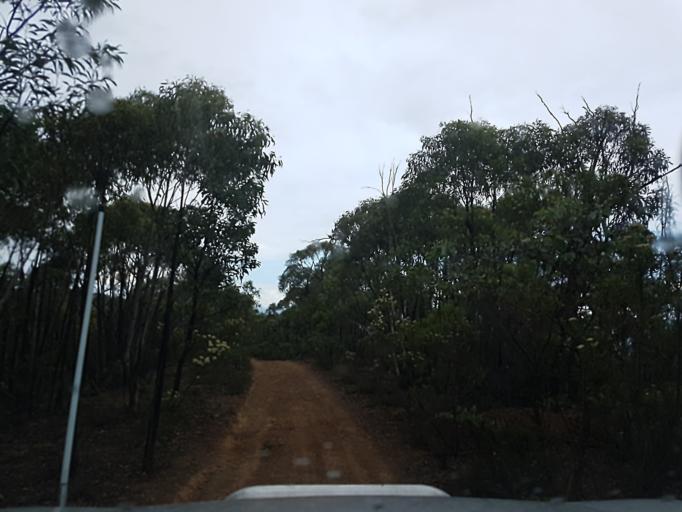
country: AU
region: New South Wales
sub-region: Snowy River
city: Jindabyne
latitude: -36.9163
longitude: 148.3369
